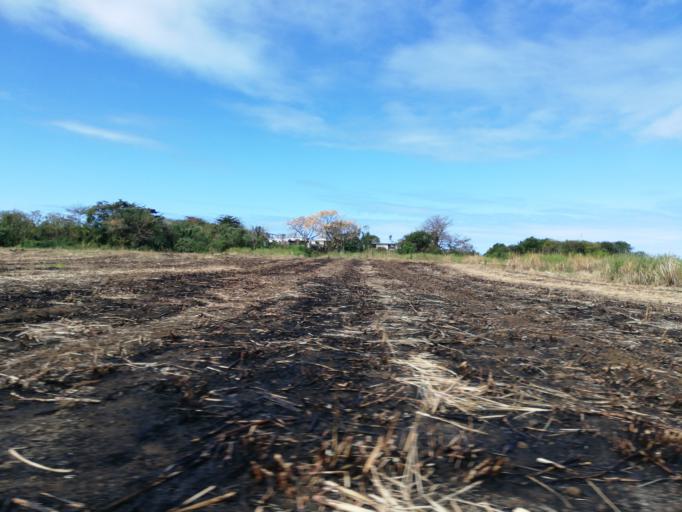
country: MU
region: Grand Port
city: Plaine Magnien
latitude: -20.4640
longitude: 57.6719
